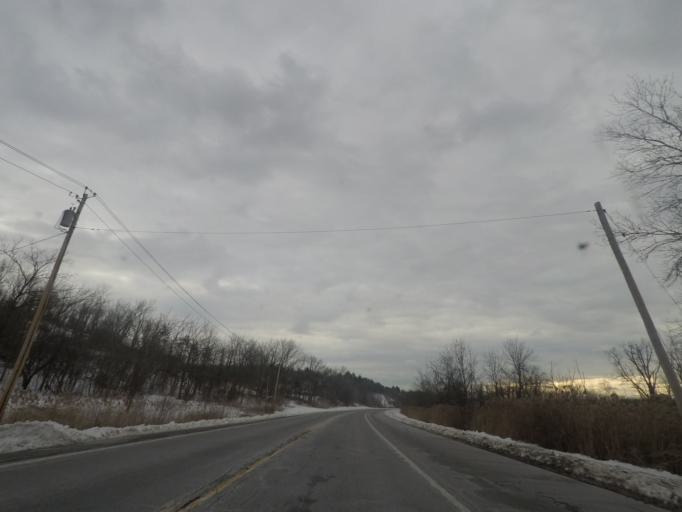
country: US
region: New York
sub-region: Rensselaer County
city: East Greenbush
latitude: 42.5740
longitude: -73.7377
